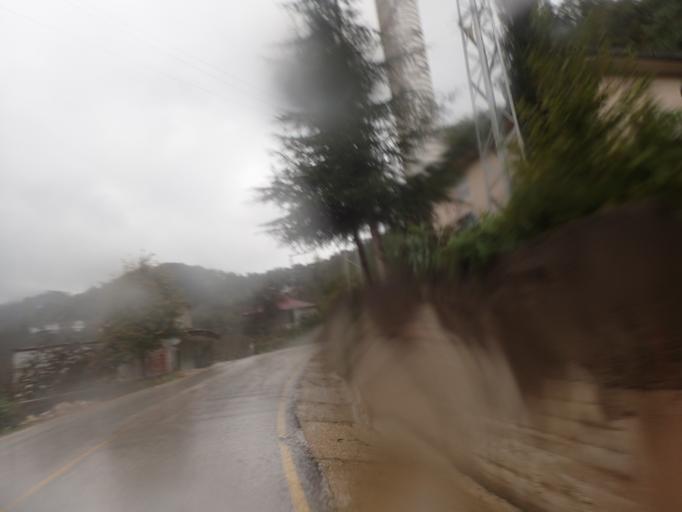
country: TR
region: Ordu
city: Persembe
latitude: 41.0429
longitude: 37.7471
